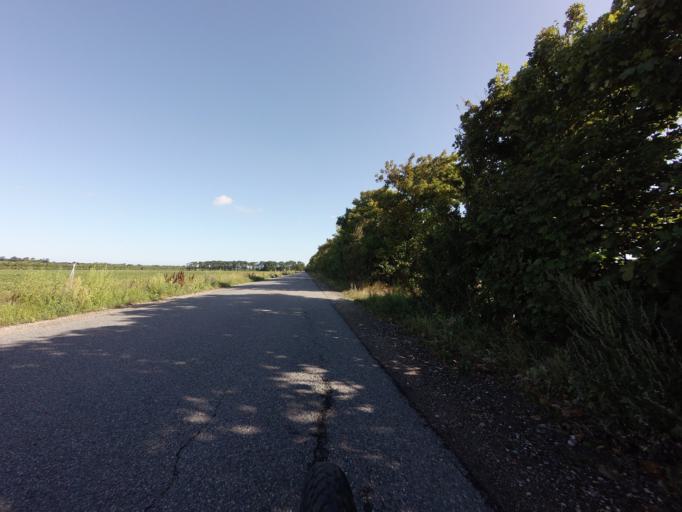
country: DK
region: North Denmark
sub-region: Hjorring Kommune
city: Vra
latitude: 57.3676
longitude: 10.0034
